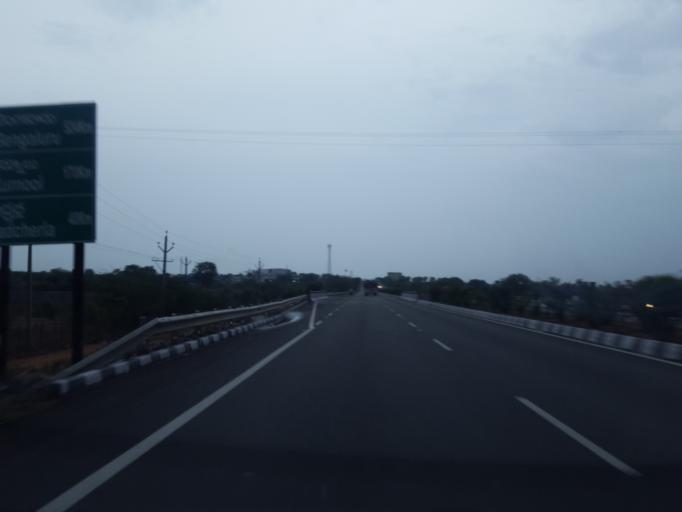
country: IN
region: Telangana
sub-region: Mahbubnagar
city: Farrukhnagar
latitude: 17.1105
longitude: 78.2620
